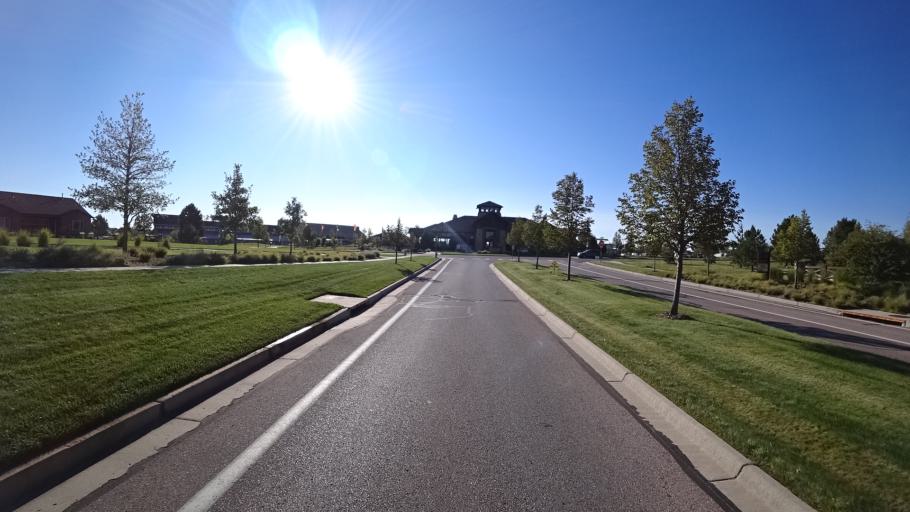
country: US
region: Colorado
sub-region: El Paso County
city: Cimarron Hills
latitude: 38.9340
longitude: -104.6776
